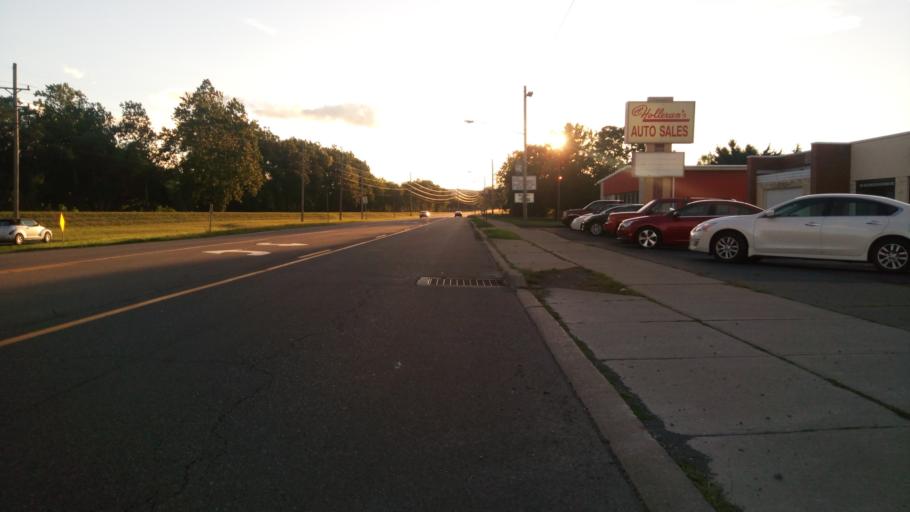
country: US
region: New York
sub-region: Chemung County
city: Southport
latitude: 42.0578
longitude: -76.8007
